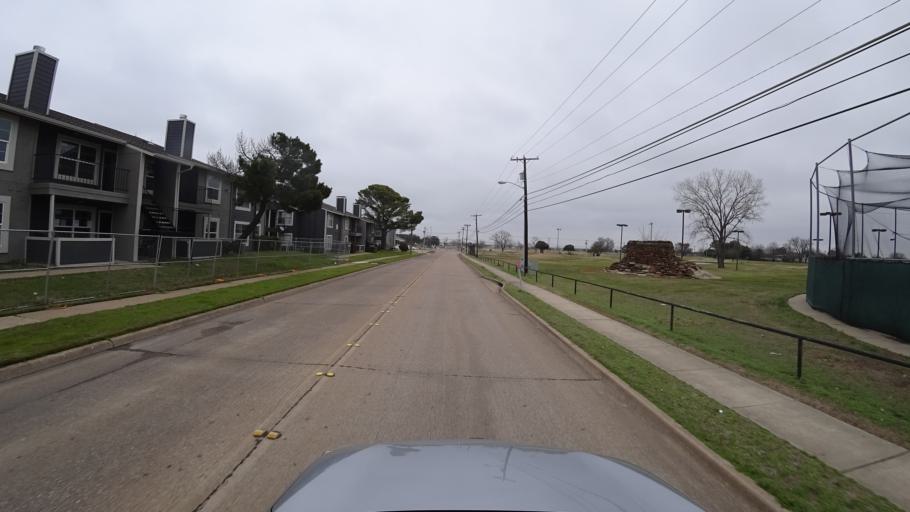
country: US
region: Texas
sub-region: Denton County
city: Lewisville
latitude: 33.0717
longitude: -97.0115
